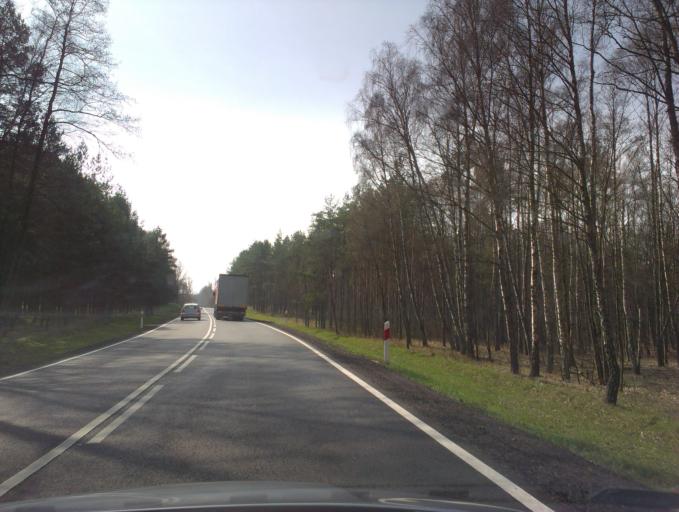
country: PL
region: Greater Poland Voivodeship
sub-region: Powiat zlotowski
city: Okonek
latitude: 53.5092
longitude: 16.8515
